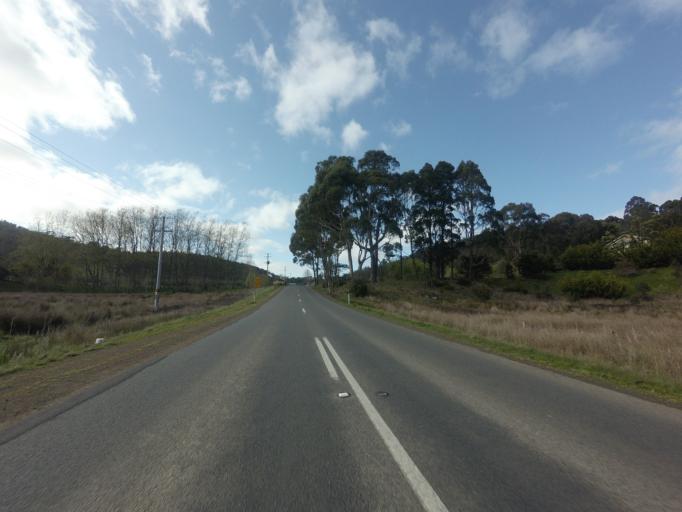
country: AU
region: Tasmania
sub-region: Huon Valley
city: Geeveston
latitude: -43.1698
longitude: 146.9418
